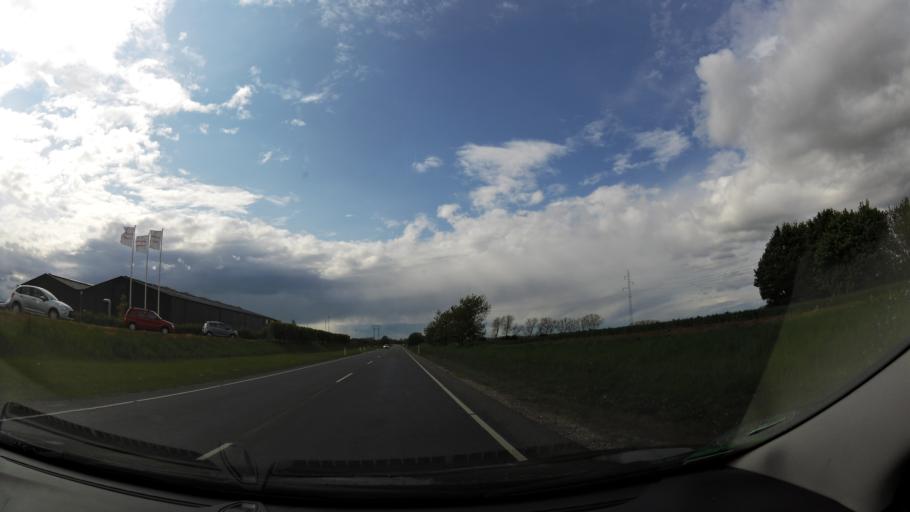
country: DK
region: South Denmark
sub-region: Nyborg Kommune
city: Nyborg
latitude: 55.3167
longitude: 10.7517
